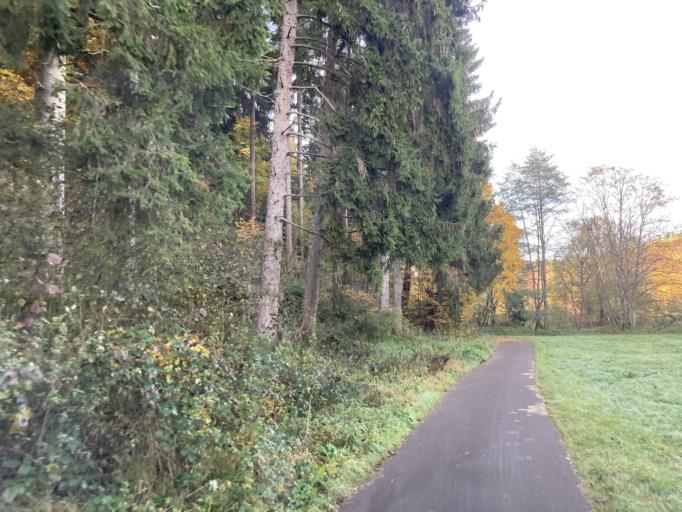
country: DE
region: Baden-Wuerttemberg
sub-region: Tuebingen Region
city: Bodelshausen
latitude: 48.4065
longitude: 8.9520
